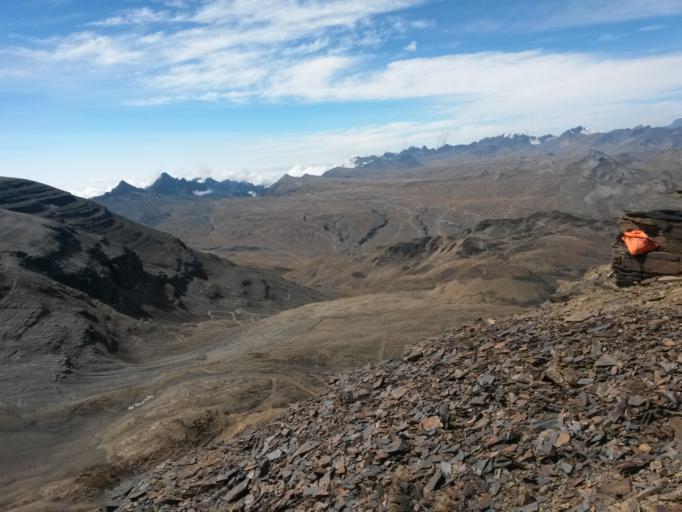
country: BO
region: La Paz
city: La Paz
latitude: -16.3488
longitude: -68.1273
